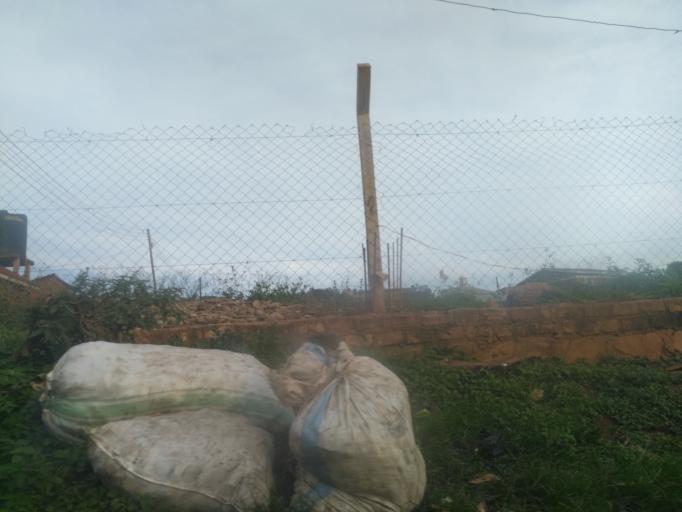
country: UG
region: Central Region
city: Kampala Central Division
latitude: 0.3421
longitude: 32.5758
